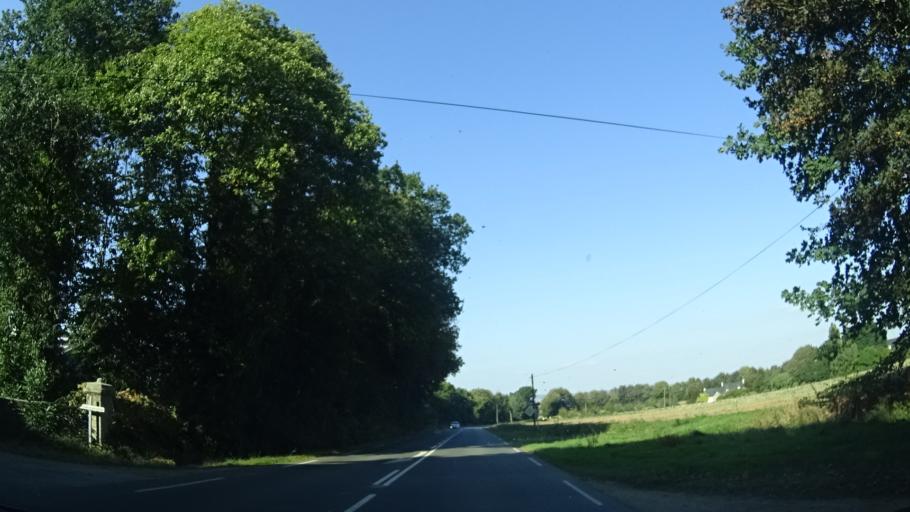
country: FR
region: Brittany
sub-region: Departement du Finistere
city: Plonevez-Porzay
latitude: 48.0960
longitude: -4.2559
